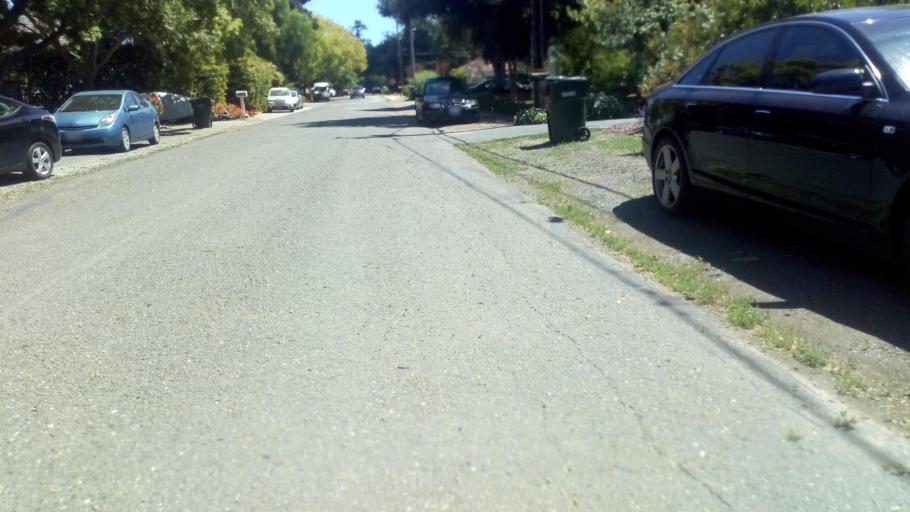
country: US
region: California
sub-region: Santa Clara County
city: Loyola
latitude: 37.3663
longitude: -122.0933
